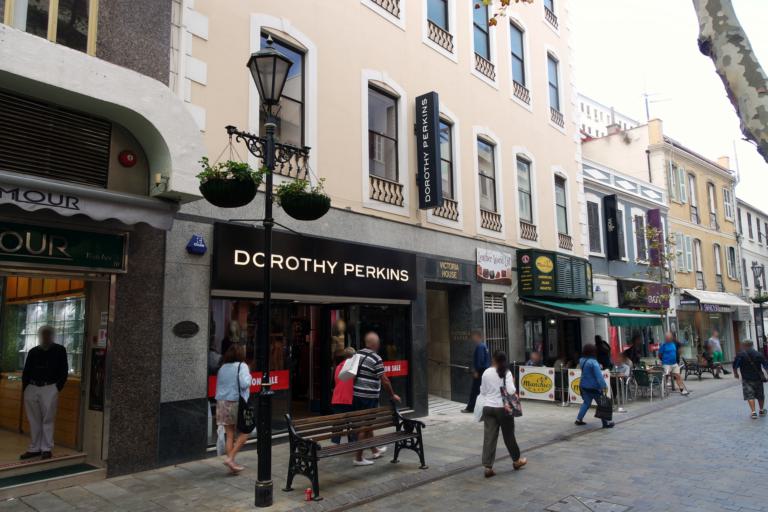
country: GI
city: Gibraltar
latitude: 36.1439
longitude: -5.3532
